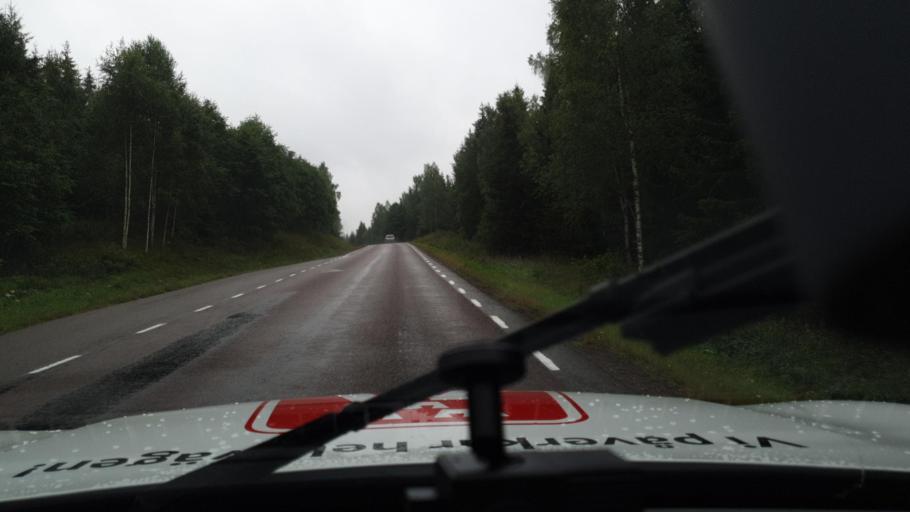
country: SE
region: Vaermland
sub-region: Torsby Kommun
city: Torsby
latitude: 59.9497
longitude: 12.7369
